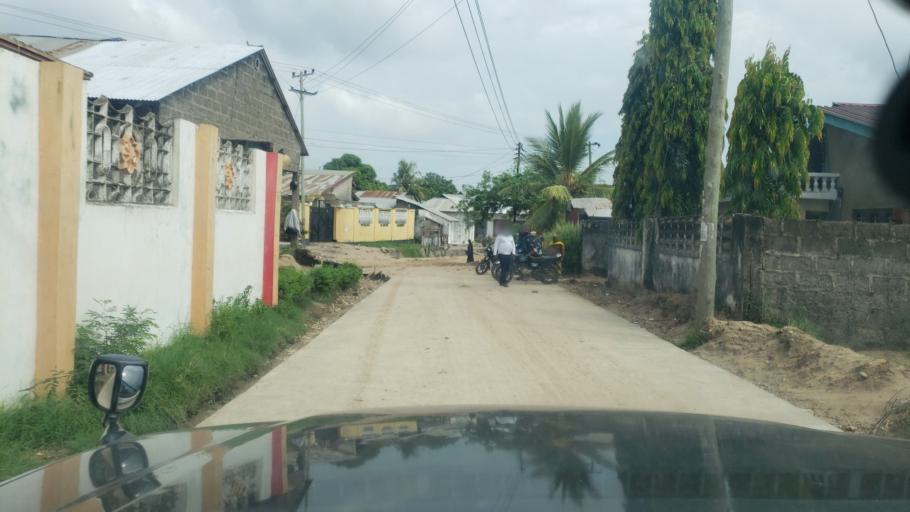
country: TZ
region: Pwani
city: Vikindu
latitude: -6.9225
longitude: 39.2549
